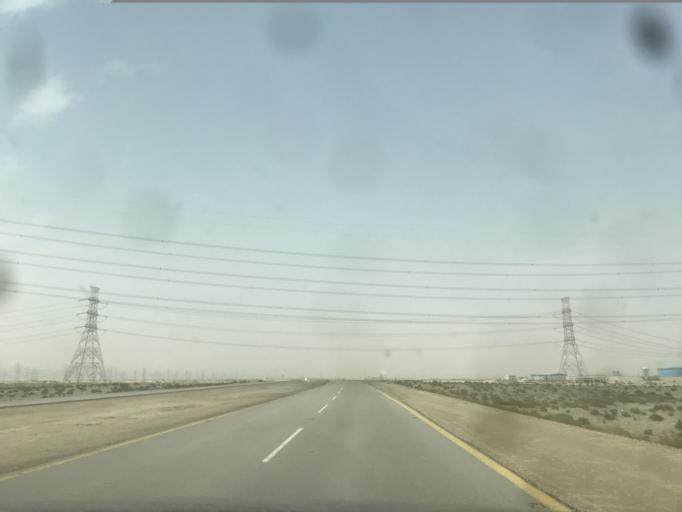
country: SA
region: Eastern Province
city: Abqaiq
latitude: 25.9106
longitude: 49.9641
